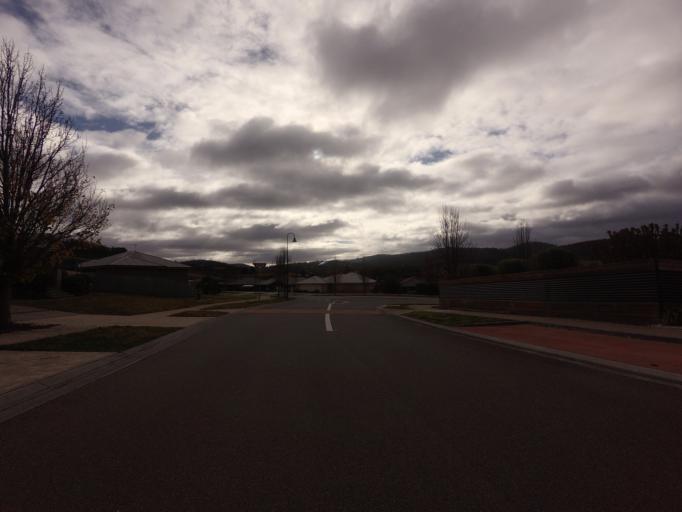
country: AU
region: Tasmania
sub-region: Clarence
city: Howrah
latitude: -42.8838
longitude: 147.4242
